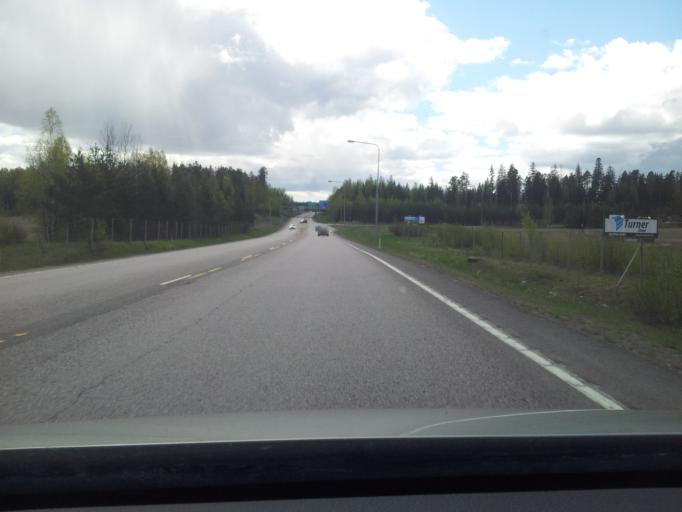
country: FI
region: Uusimaa
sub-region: Loviisa
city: Perna
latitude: 60.5009
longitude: 25.9634
